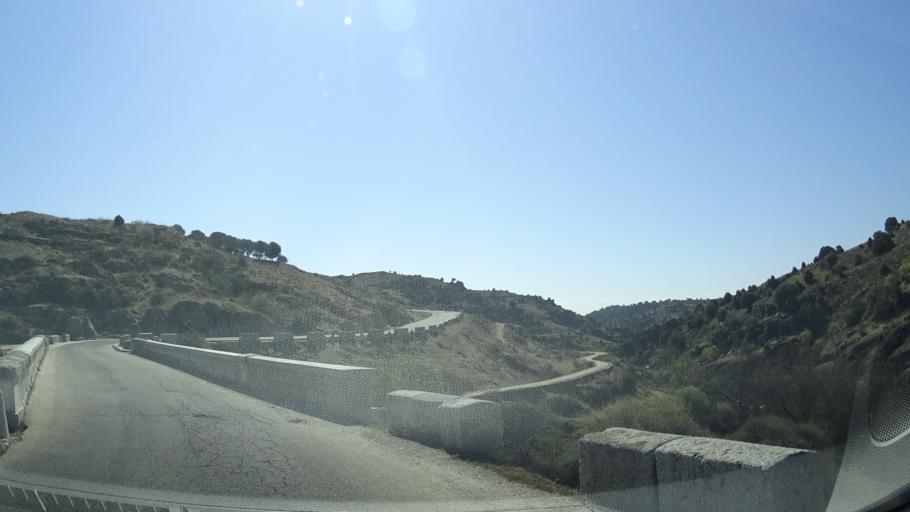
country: ES
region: Madrid
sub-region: Provincia de Madrid
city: Colmenar Viejo
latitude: 40.6483
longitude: -3.8089
